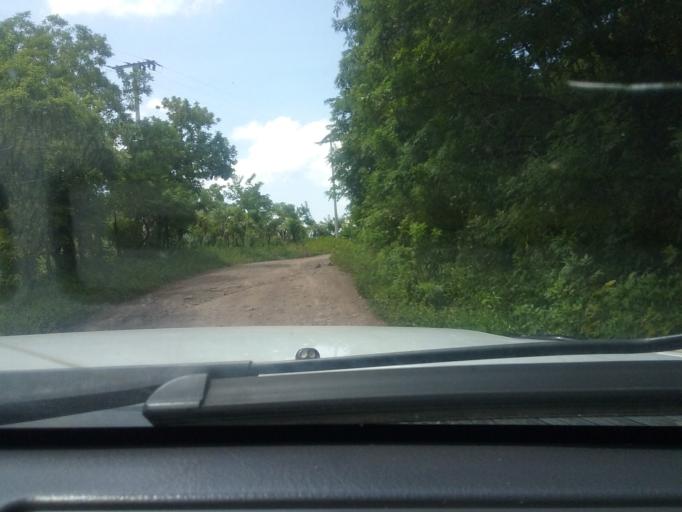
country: NI
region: Matagalpa
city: Terrabona
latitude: 12.6978
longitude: -85.9507
